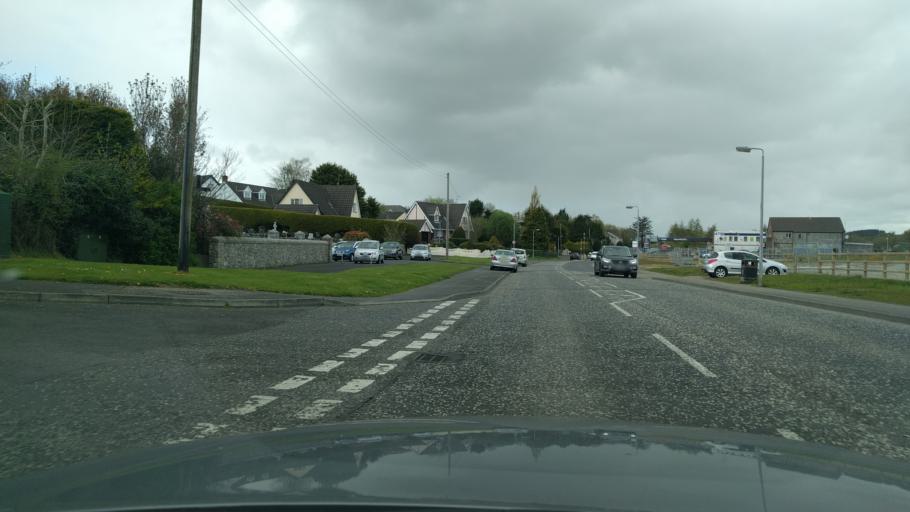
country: GB
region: Northern Ireland
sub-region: Down District
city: Warrenpoint
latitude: 54.1114
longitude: -6.2581
